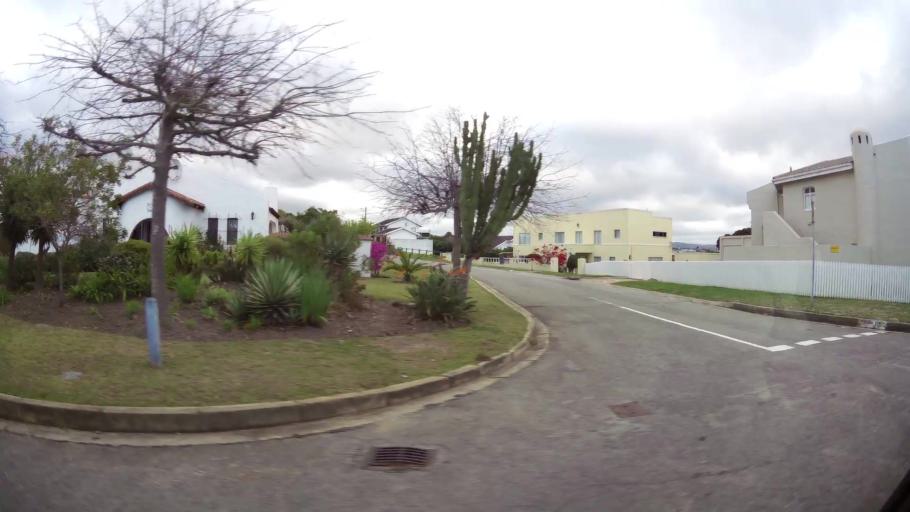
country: ZA
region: Western Cape
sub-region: Eden District Municipality
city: Plettenberg Bay
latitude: -34.0520
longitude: 23.3683
